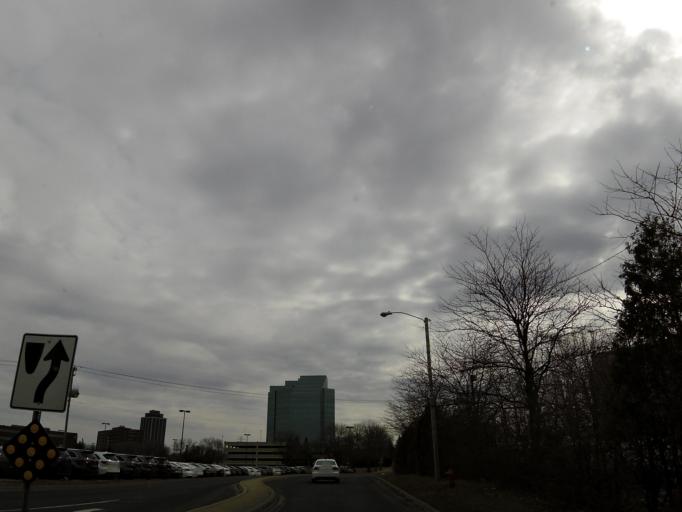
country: US
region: Minnesota
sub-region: Hennepin County
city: Edina
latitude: 44.8630
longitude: -93.3347
